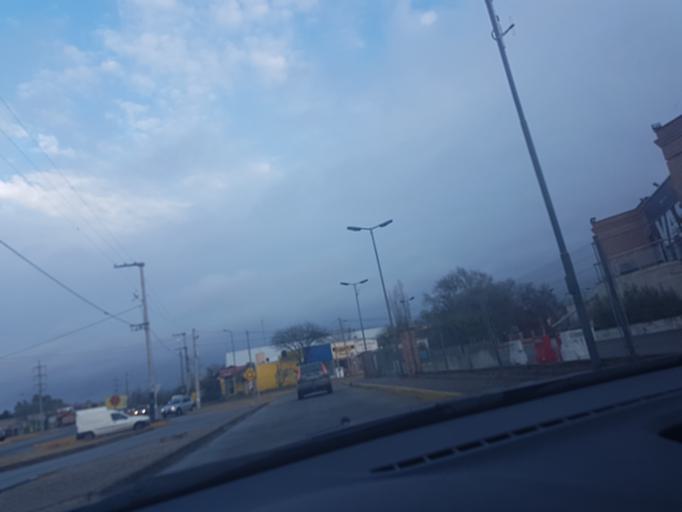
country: AR
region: Cordoba
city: Villa Allende
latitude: -31.3004
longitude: -64.2774
